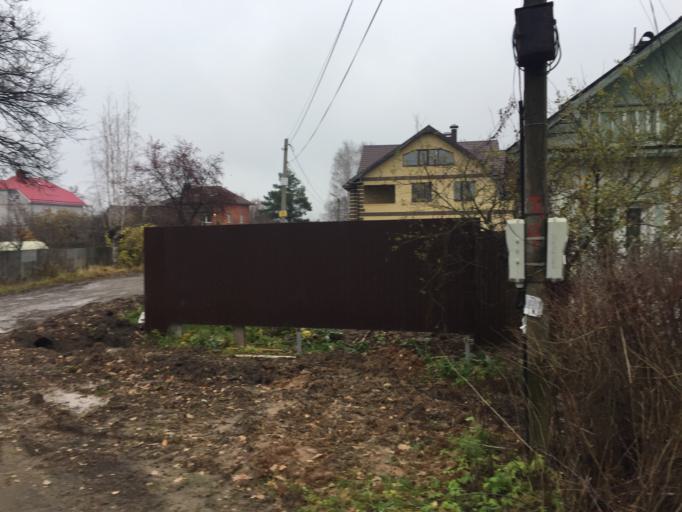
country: RU
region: Jaroslavl
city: Yaroslavl
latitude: 57.7240
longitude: 39.7695
